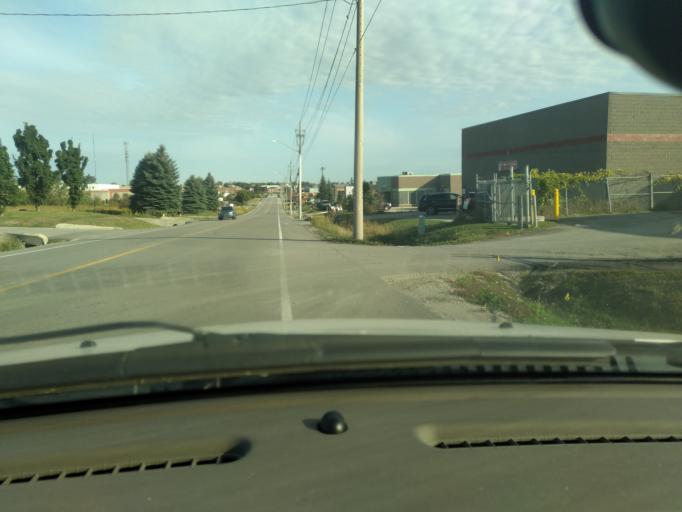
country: CA
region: Ontario
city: Innisfil
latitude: 44.3252
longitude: -79.6795
